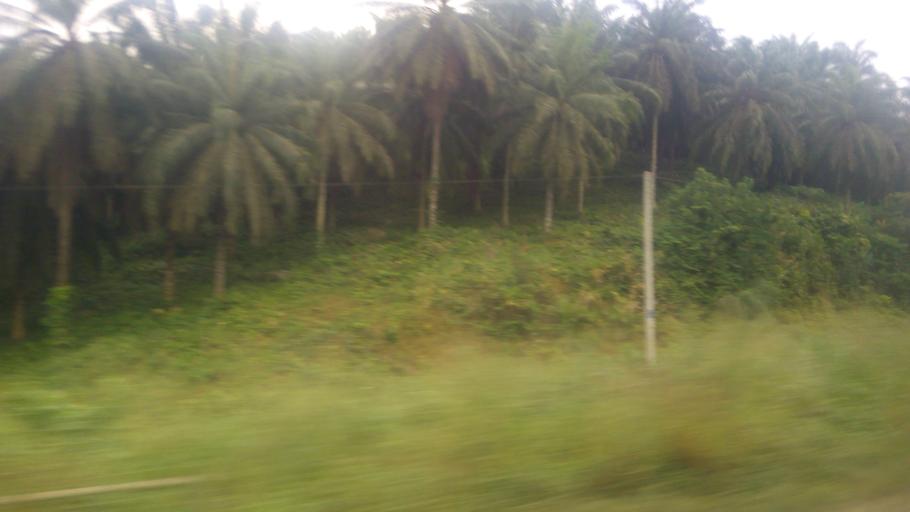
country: GH
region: Western
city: Takoradi
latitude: 4.8920
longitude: -1.8870
